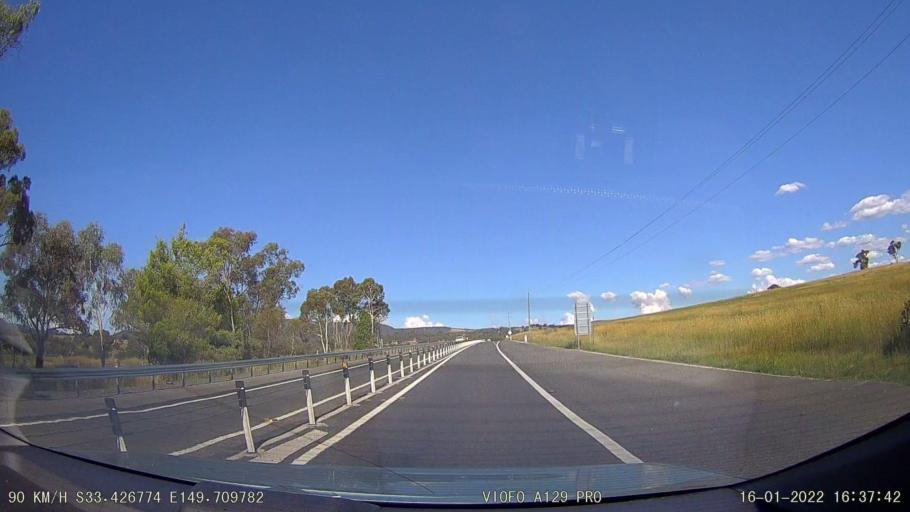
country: AU
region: New South Wales
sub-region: Bathurst Regional
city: Kelso
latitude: -33.4264
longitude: 149.7092
